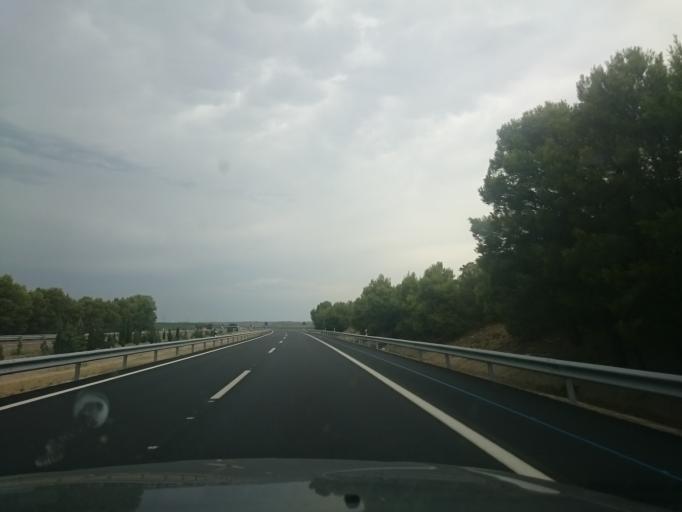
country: ES
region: Aragon
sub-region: Provincia de Zaragoza
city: Pina de Ebro
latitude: 41.5333
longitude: -0.5127
